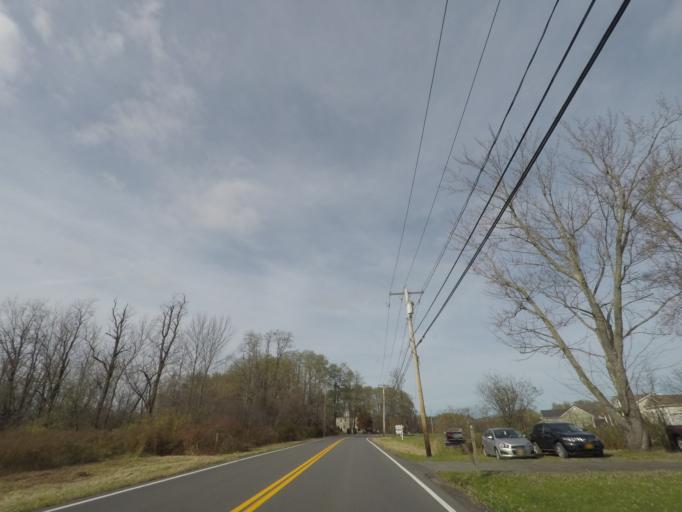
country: US
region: New York
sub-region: Schenectady County
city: Rotterdam
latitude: 42.7558
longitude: -73.9863
